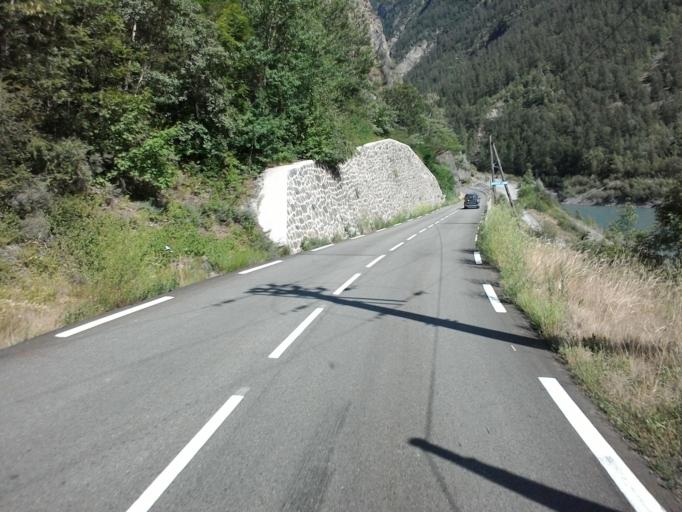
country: FR
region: Rhone-Alpes
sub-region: Departement de l'Isere
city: Mont-de-Lans
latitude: 45.0413
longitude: 6.1719
